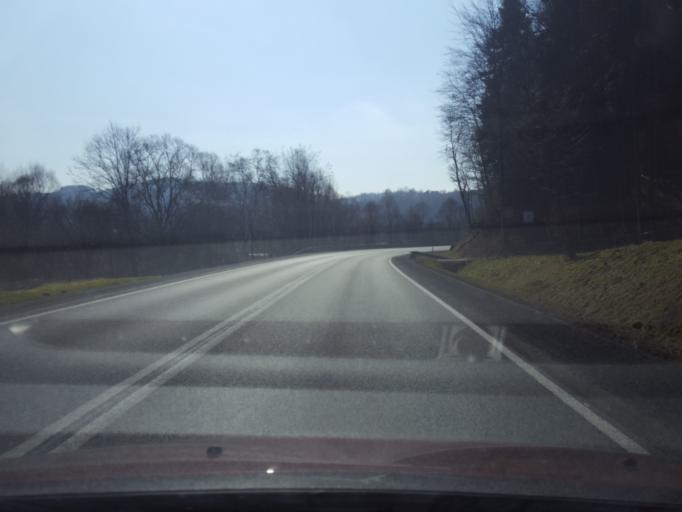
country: PL
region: Lesser Poland Voivodeship
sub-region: Powiat nowosadecki
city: Lososina Dolna
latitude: 49.7917
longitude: 20.6490
